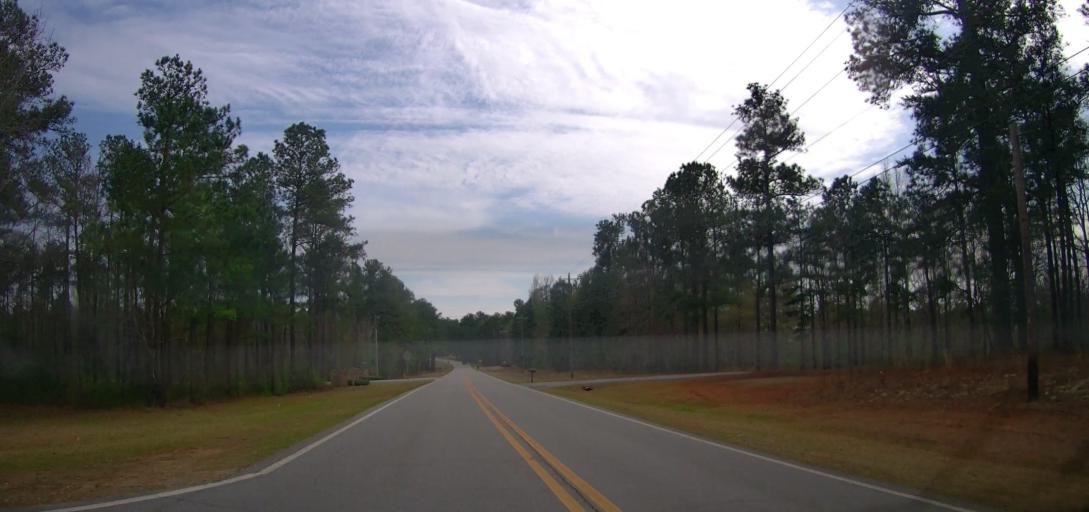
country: US
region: Georgia
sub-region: Bibb County
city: Macon
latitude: 32.9500
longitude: -83.6499
